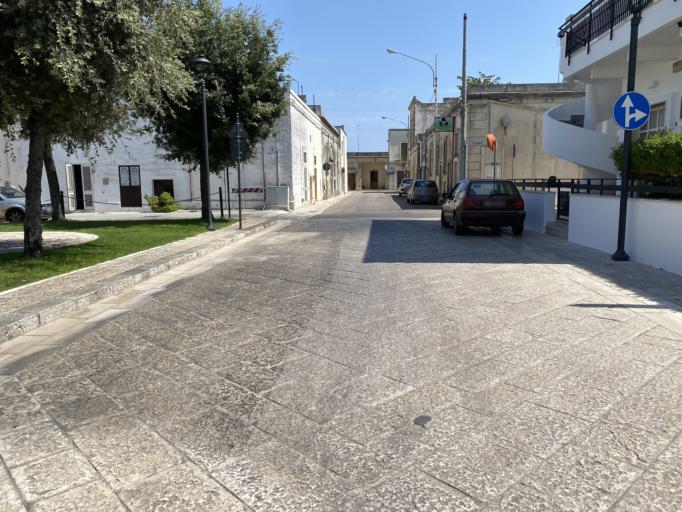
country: IT
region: Apulia
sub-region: Provincia di Lecce
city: Muro Leccese
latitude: 40.0977
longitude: 18.3395
